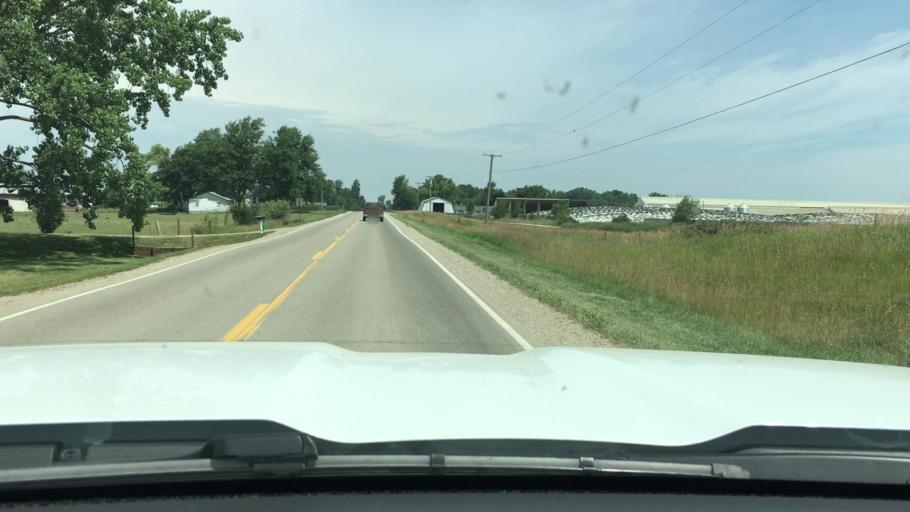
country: US
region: Michigan
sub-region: Sanilac County
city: Marlette
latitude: 43.3107
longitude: -82.9837
